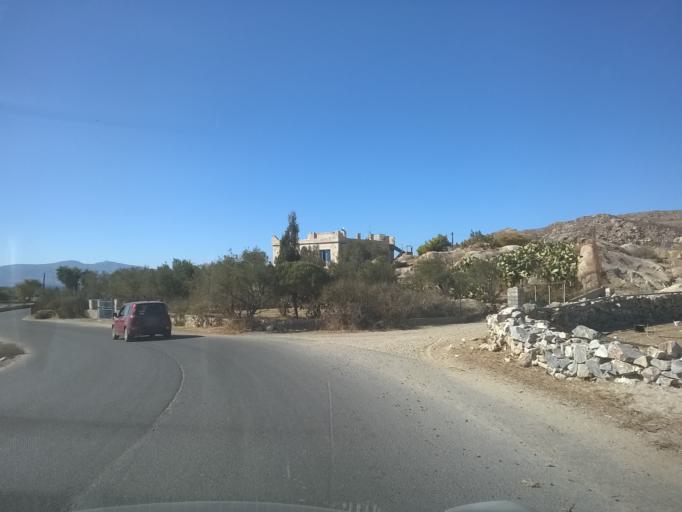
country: GR
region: South Aegean
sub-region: Nomos Kykladon
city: Naxos
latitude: 37.0177
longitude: 25.3908
